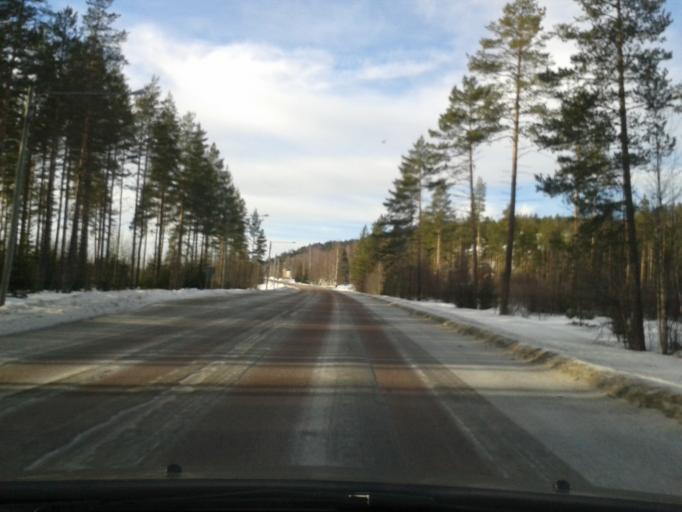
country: SE
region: Vaesternorrland
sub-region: OErnskoeldsviks Kommun
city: Bjasta
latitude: 63.3802
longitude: 18.4157
